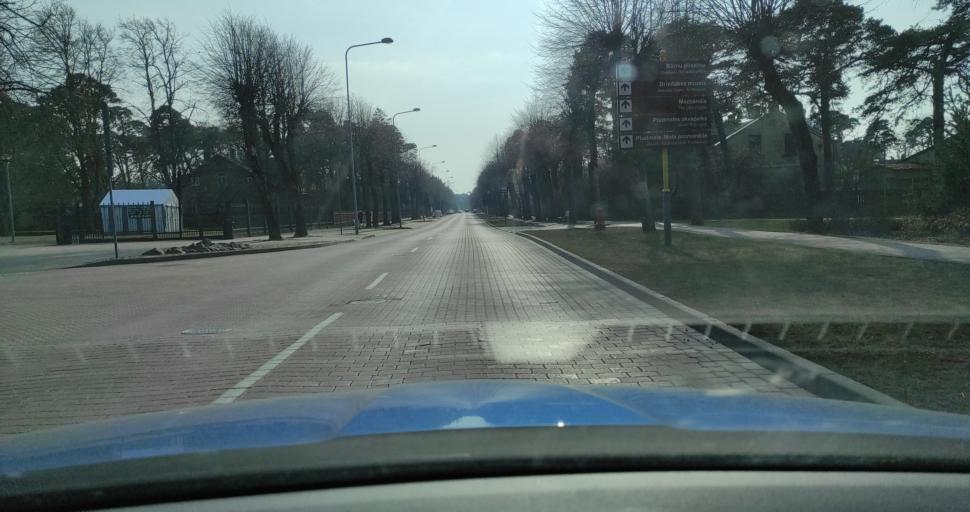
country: LV
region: Ventspils
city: Ventspils
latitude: 57.3898
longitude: 21.5463
